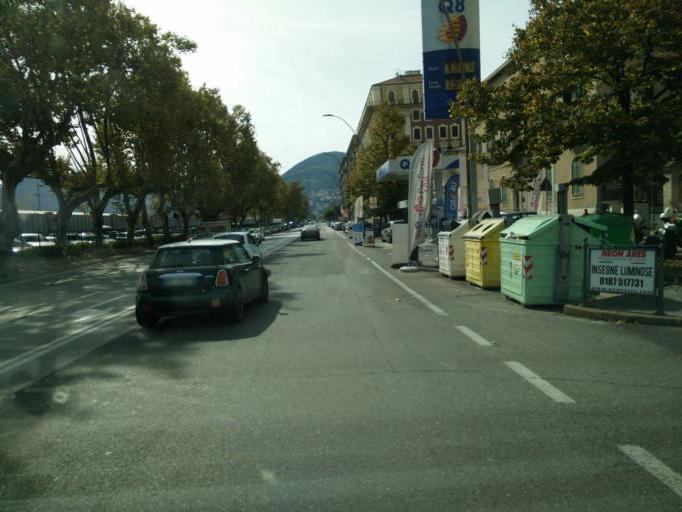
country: IT
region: Liguria
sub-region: Provincia di La Spezia
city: La Spezia
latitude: 44.1095
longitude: 9.8329
